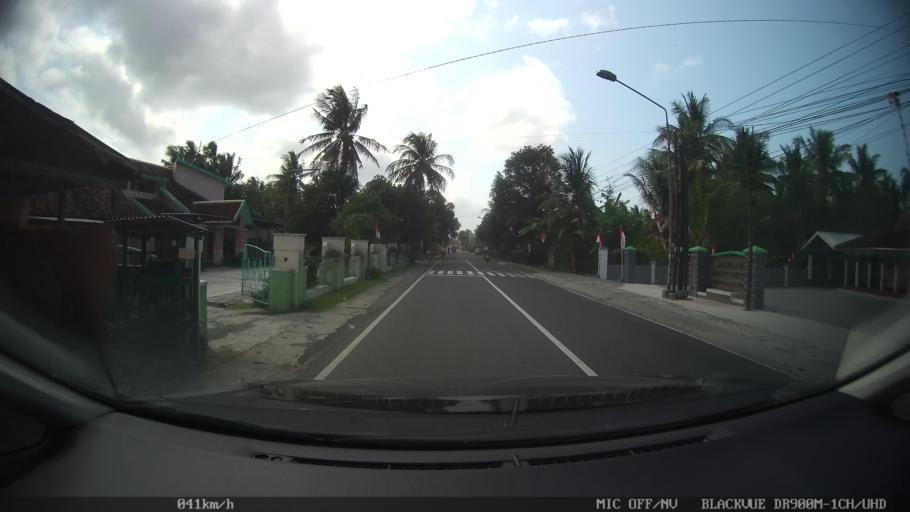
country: ID
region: Daerah Istimewa Yogyakarta
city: Srandakan
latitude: -7.8930
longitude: 110.1363
